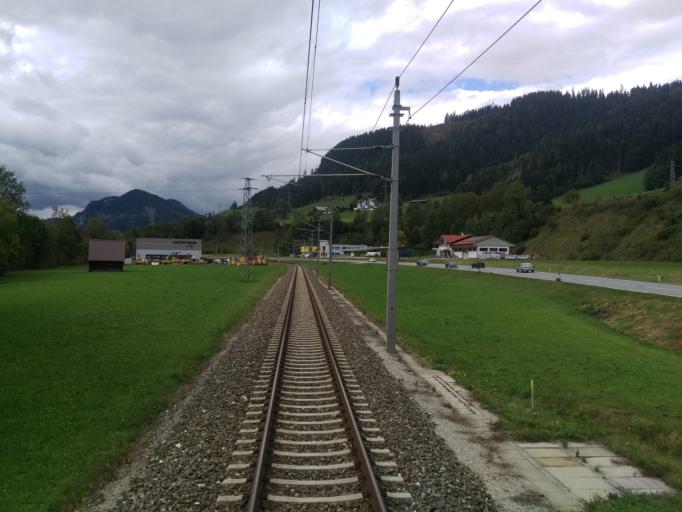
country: AT
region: Styria
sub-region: Politischer Bezirk Liezen
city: Schladming
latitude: 47.3885
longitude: 13.6467
